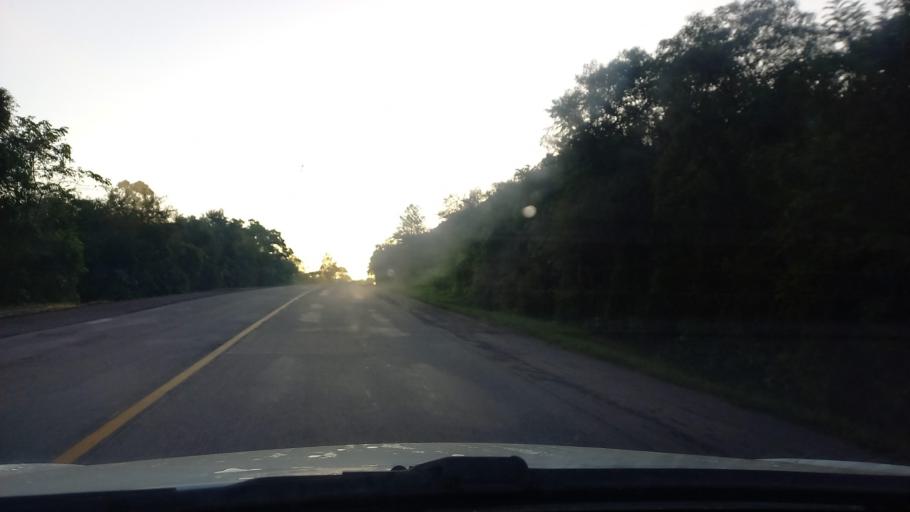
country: BR
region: Rio Grande do Sul
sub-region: Candelaria
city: Candelaria
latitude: -29.6833
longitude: -52.8443
